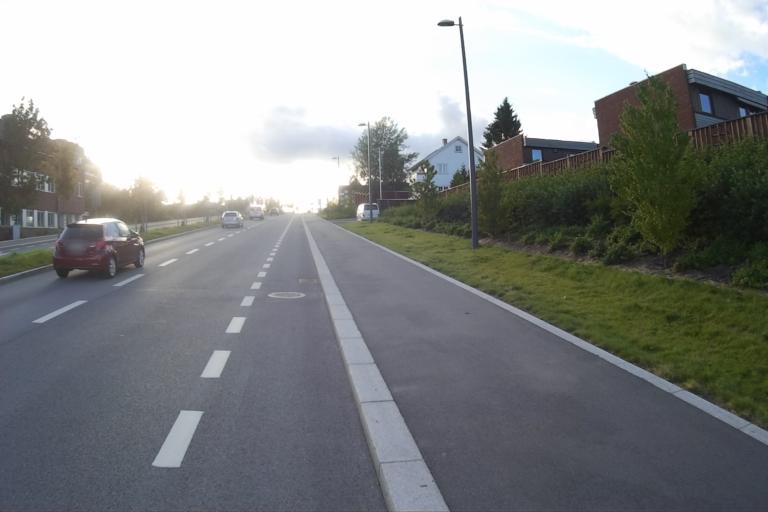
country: NO
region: Oslo
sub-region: Oslo
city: Oslo
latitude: 59.9337
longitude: 10.7951
